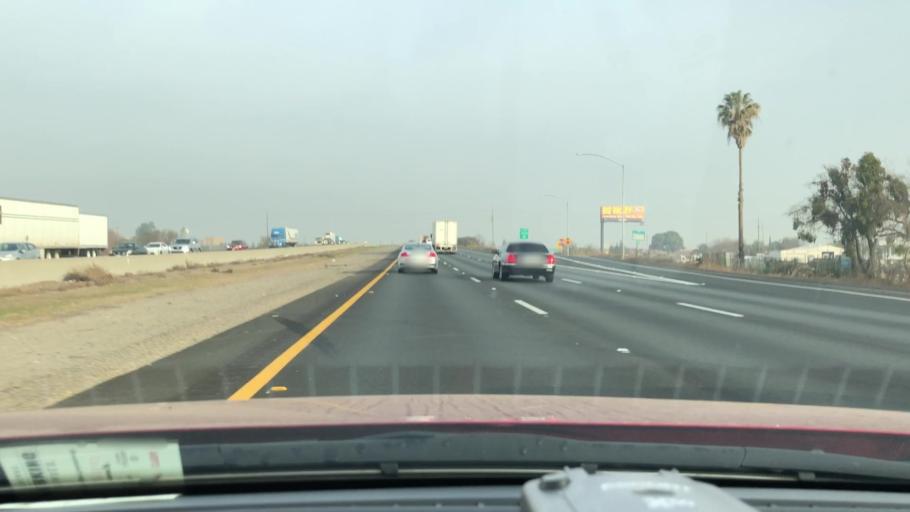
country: US
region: California
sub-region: San Joaquin County
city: French Camp
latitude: 37.8789
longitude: -121.2783
